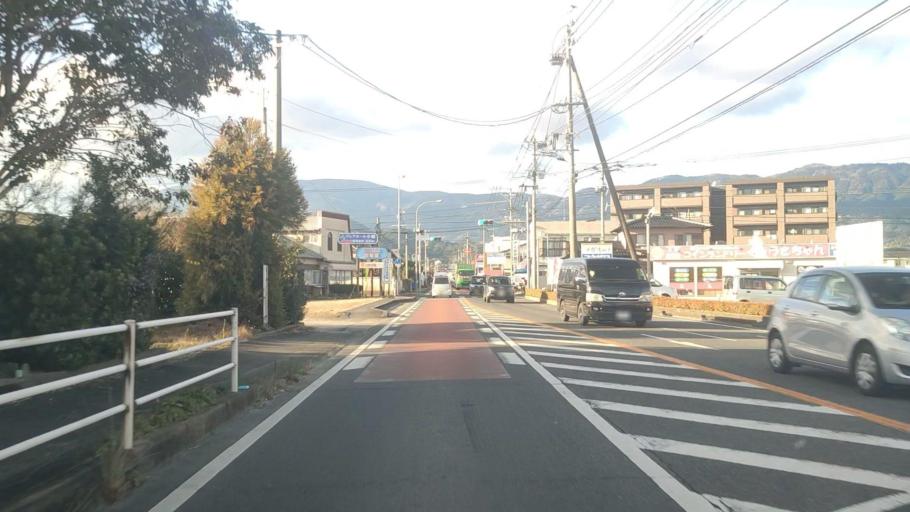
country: JP
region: Saga Prefecture
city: Saga-shi
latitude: 33.2872
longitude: 130.2071
